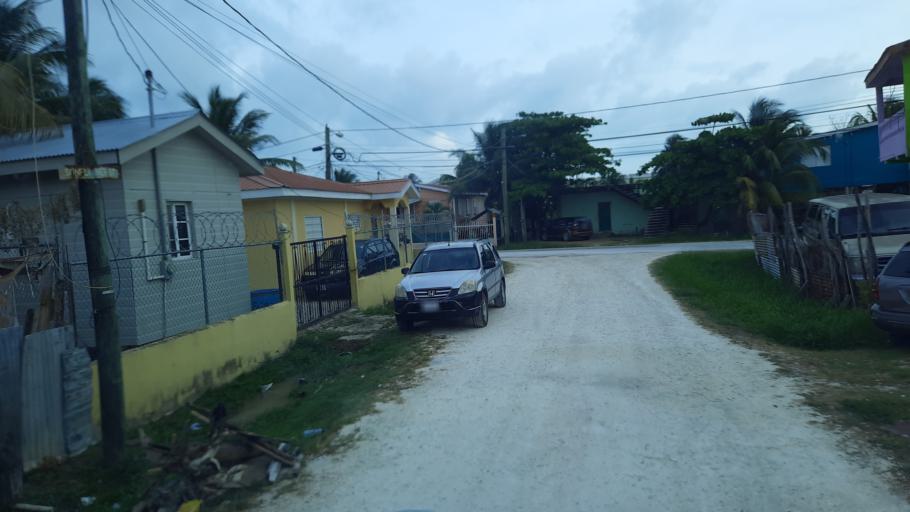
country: BZ
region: Belize
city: Belize City
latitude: 17.5013
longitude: -88.2067
